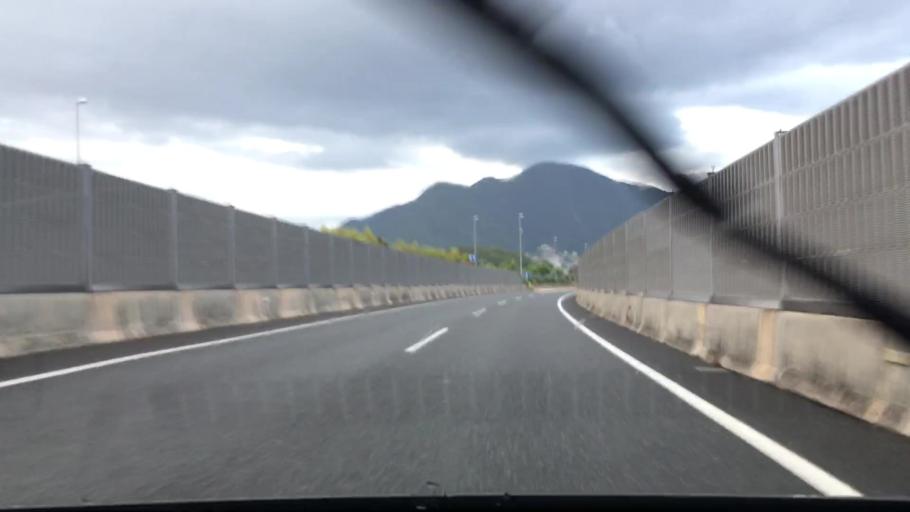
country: JP
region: Fukuoka
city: Kitakyushu
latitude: 33.8204
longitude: 130.8867
